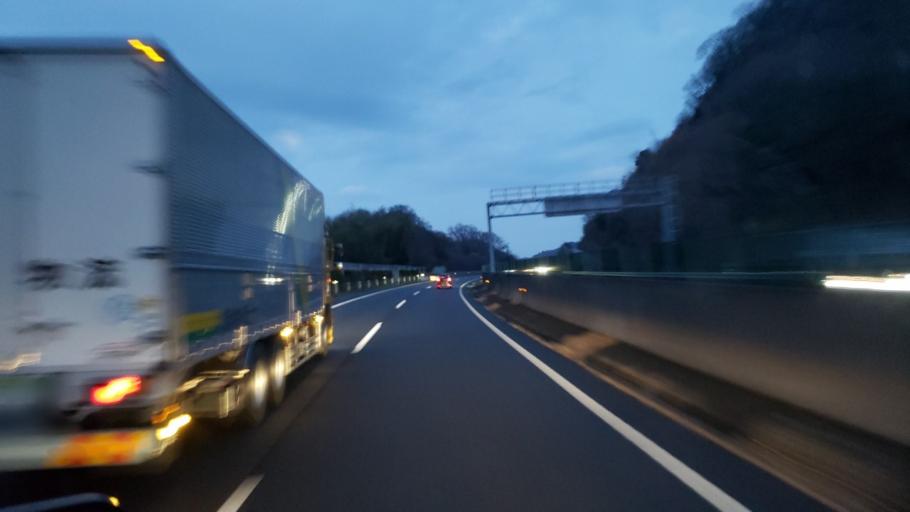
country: JP
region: Hyogo
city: Himeji
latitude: 34.8512
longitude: 134.7603
